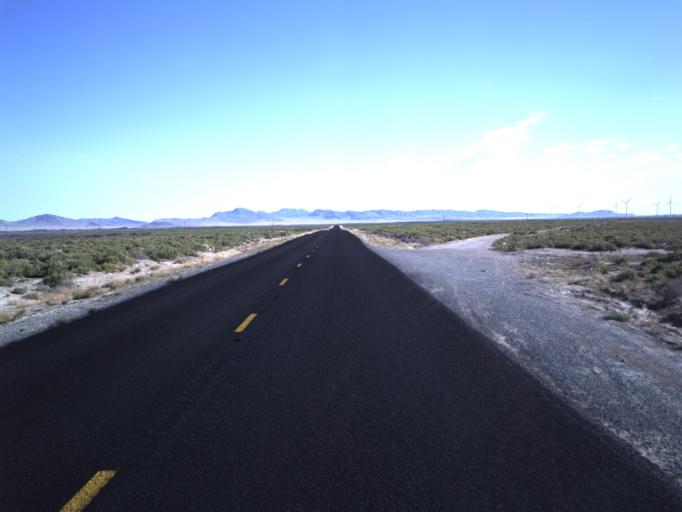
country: US
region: Utah
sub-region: Beaver County
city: Milford
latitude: 38.5395
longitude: -112.9912
